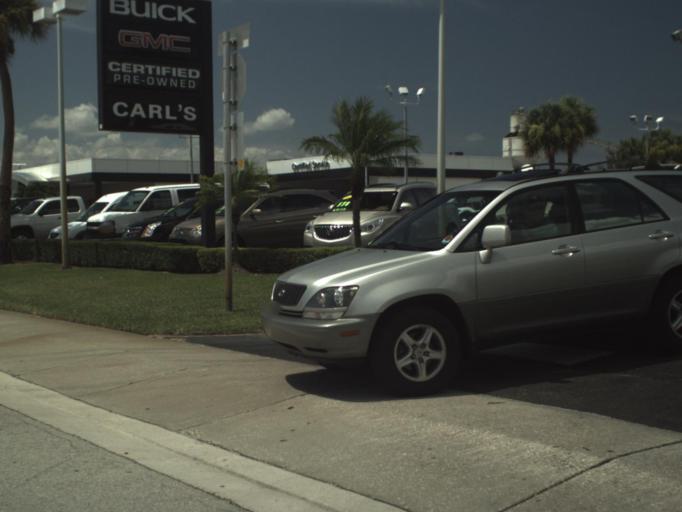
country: US
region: Florida
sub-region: Martin County
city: Stuart
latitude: 27.1742
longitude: -80.2329
